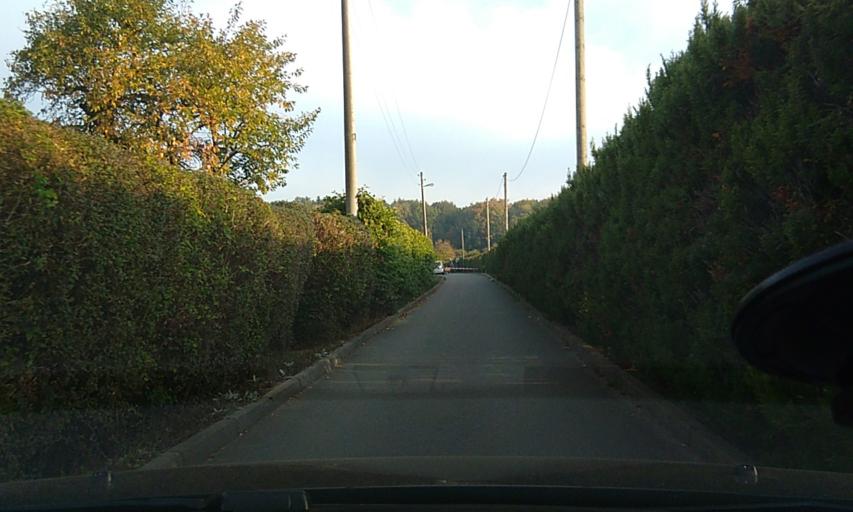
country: DE
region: Saxony
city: Wittgensdorf
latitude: 50.8475
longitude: 12.8691
